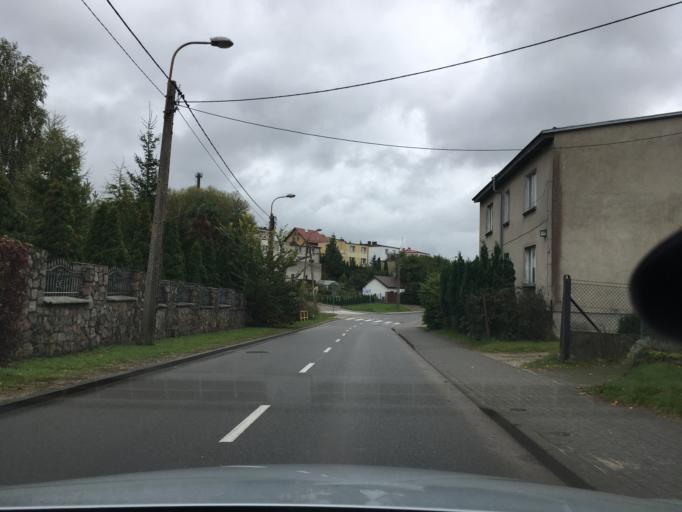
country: PL
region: Pomeranian Voivodeship
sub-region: Powiat koscierski
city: Koscierzyna
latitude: 54.1191
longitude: 17.9858
